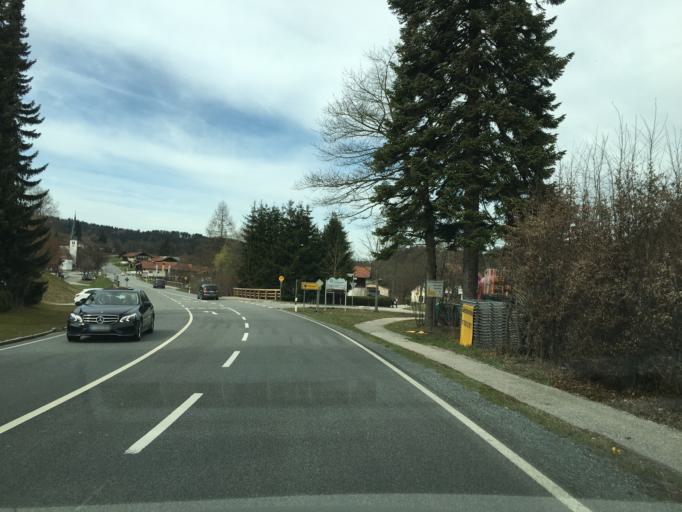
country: DE
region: Bavaria
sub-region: Upper Bavaria
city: Inzell
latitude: 47.8002
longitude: 12.7071
